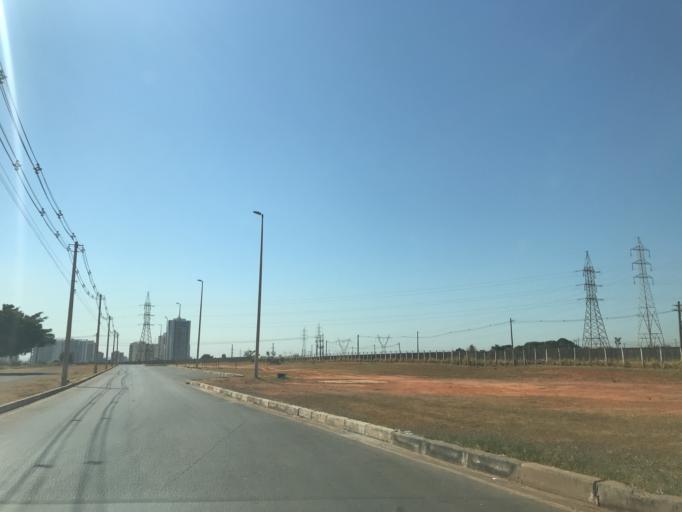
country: BR
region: Federal District
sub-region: Brasilia
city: Brasilia
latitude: -15.8504
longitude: -48.0403
